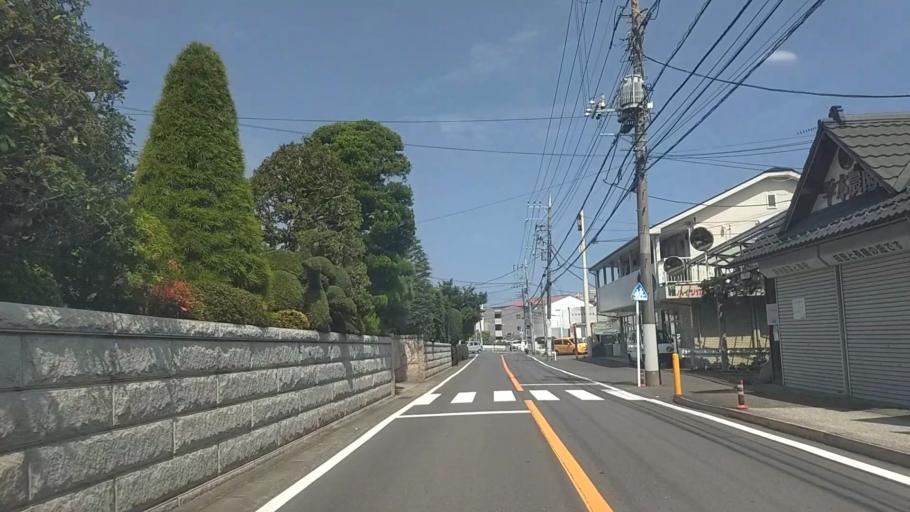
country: JP
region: Kanagawa
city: Yokohama
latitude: 35.4937
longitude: 139.5980
